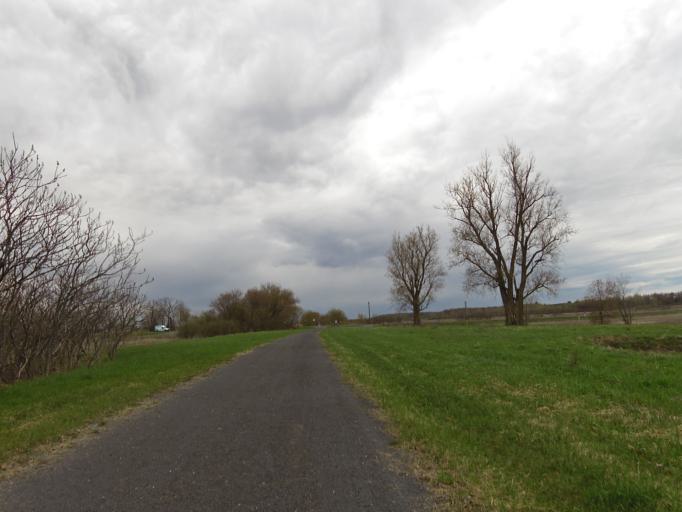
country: CA
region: Quebec
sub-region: Outaouais
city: Papineauville
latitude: 45.5303
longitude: -74.8911
